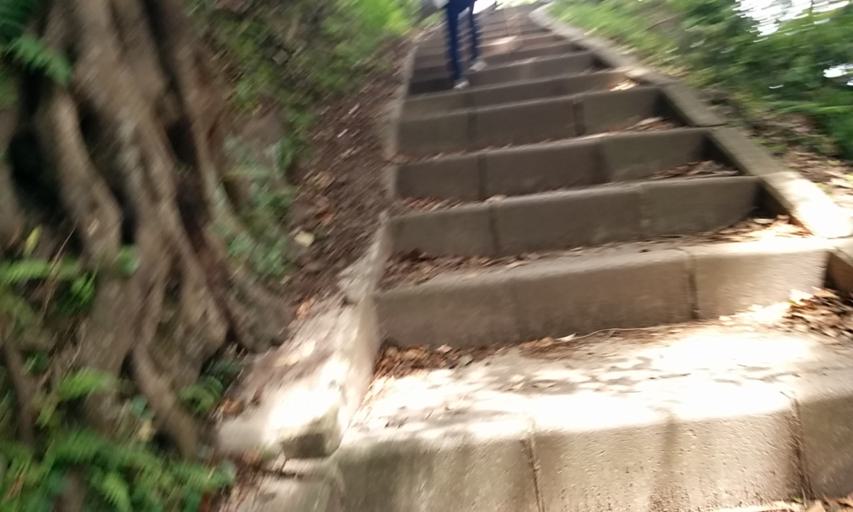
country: JP
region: Kyoto
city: Miyazu
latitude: 35.7747
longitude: 135.2241
